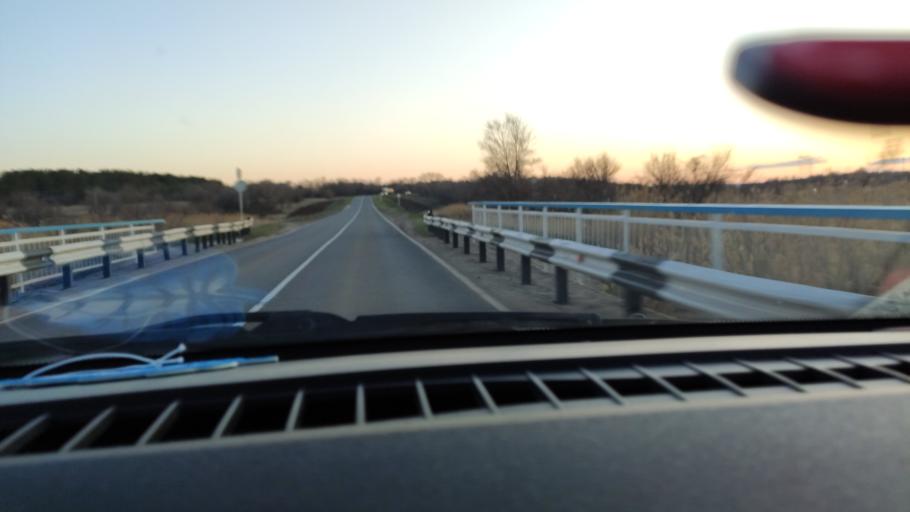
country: RU
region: Saratov
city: Privolzhskiy
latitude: 51.2896
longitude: 45.9827
